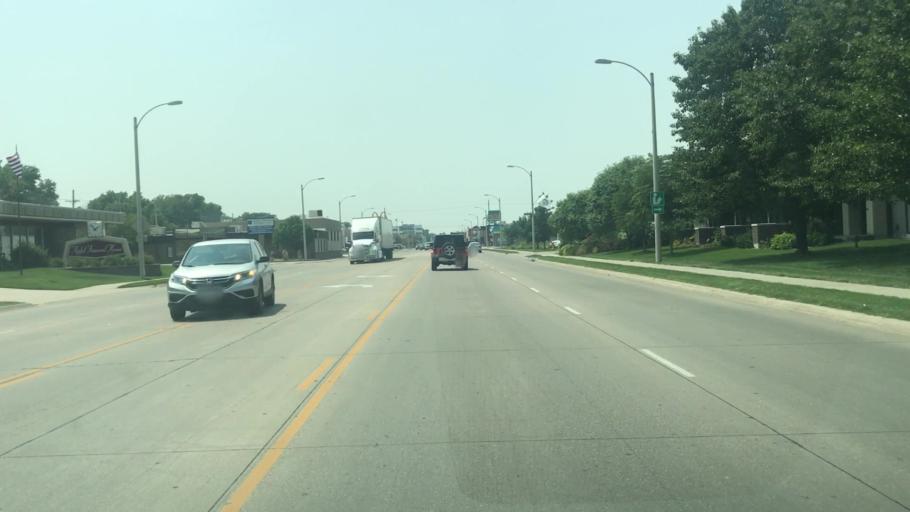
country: US
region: Nebraska
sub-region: Hall County
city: Grand Island
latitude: 40.9205
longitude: -98.3507
